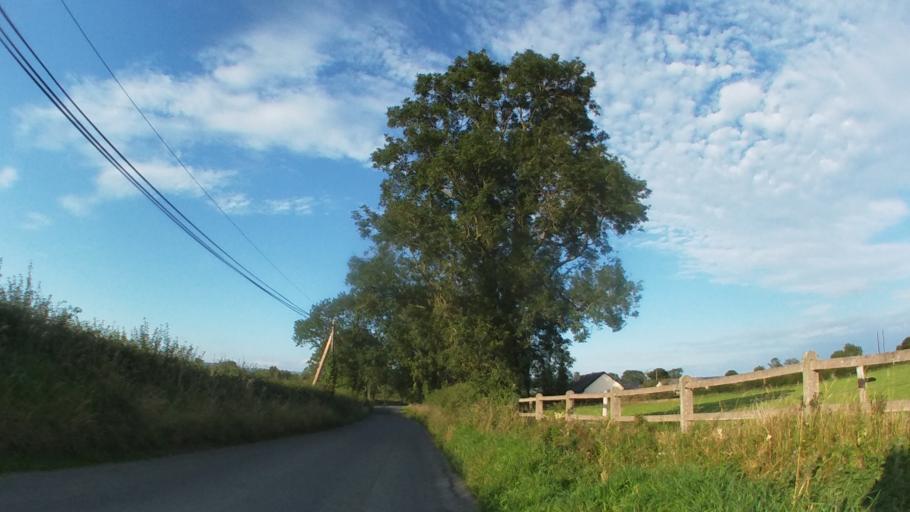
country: IE
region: Leinster
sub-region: Kilkenny
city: Kilkenny
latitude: 52.6675
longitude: -7.2175
